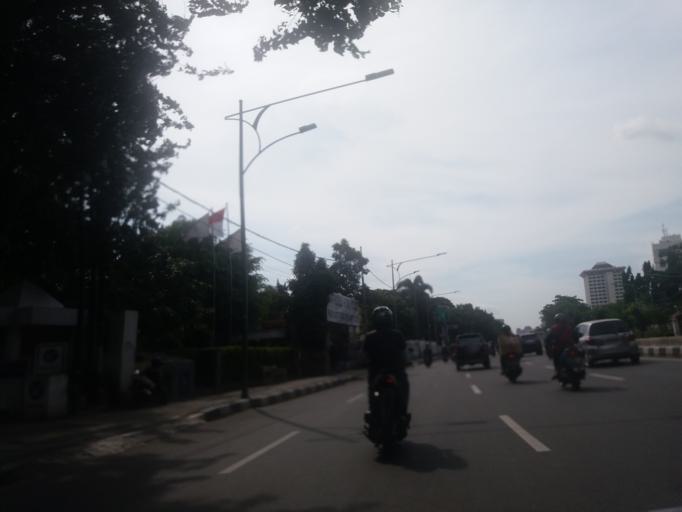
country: ID
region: Jakarta Raya
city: Jakarta
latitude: -6.1817
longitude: 106.8328
